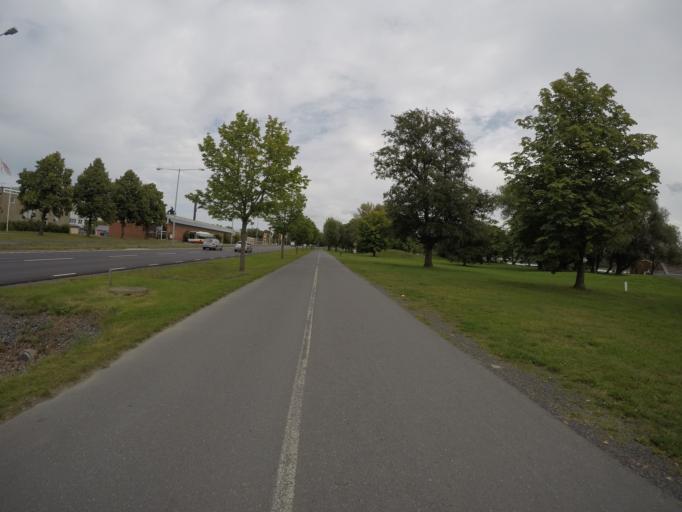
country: SE
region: Joenkoeping
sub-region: Jonkopings Kommun
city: Jonkoping
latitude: 57.7791
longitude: 14.1890
